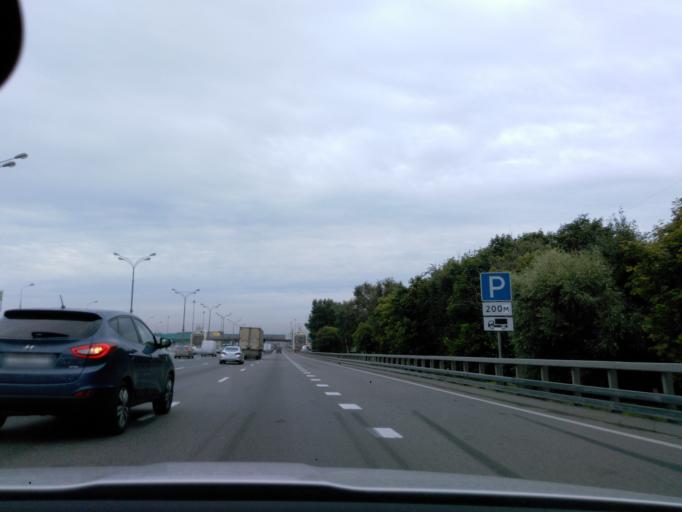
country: RU
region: Moskovskaya
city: Kuskovo
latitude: 55.7359
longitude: 37.8406
